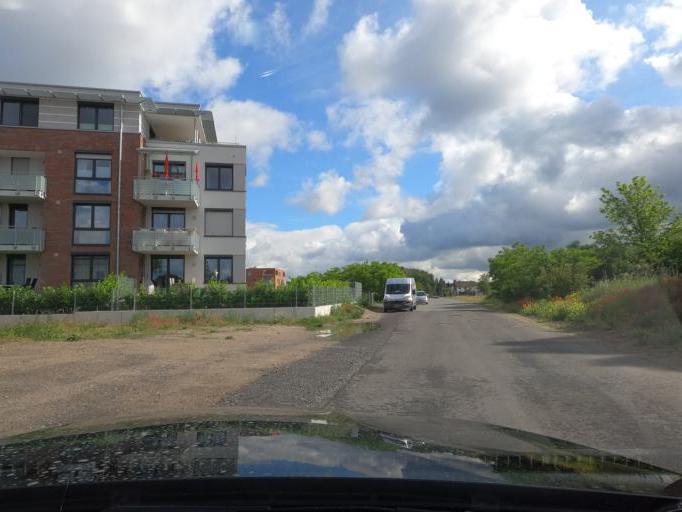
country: DE
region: Lower Saxony
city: Isernhagen Farster Bauerschaft
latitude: 52.3899
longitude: 9.8388
